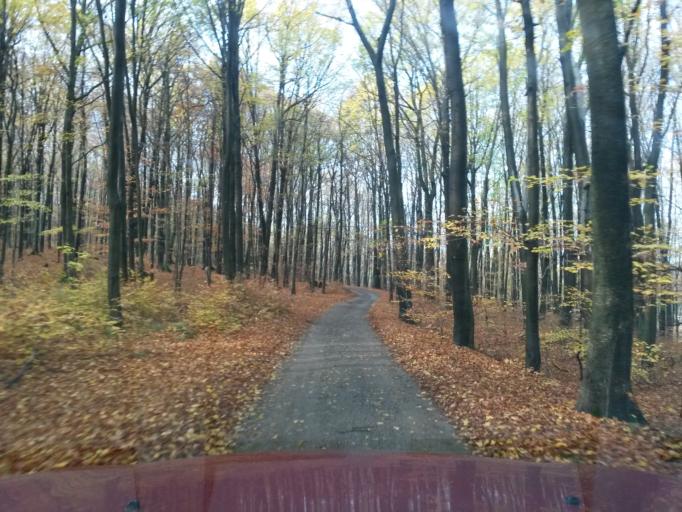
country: SK
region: Kosicky
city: Kosice
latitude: 48.7575
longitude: 21.2198
